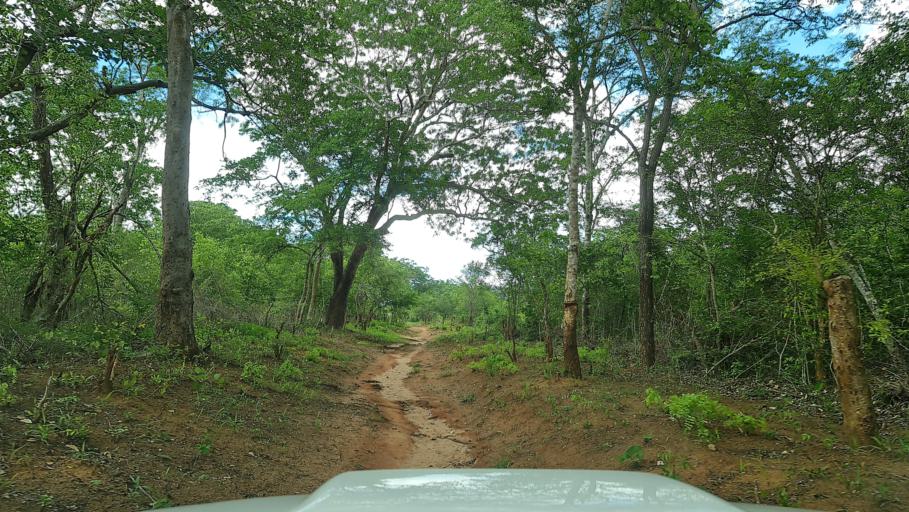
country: MZ
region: Nampula
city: Ilha de Mocambique
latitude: -15.5051
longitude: 40.1874
